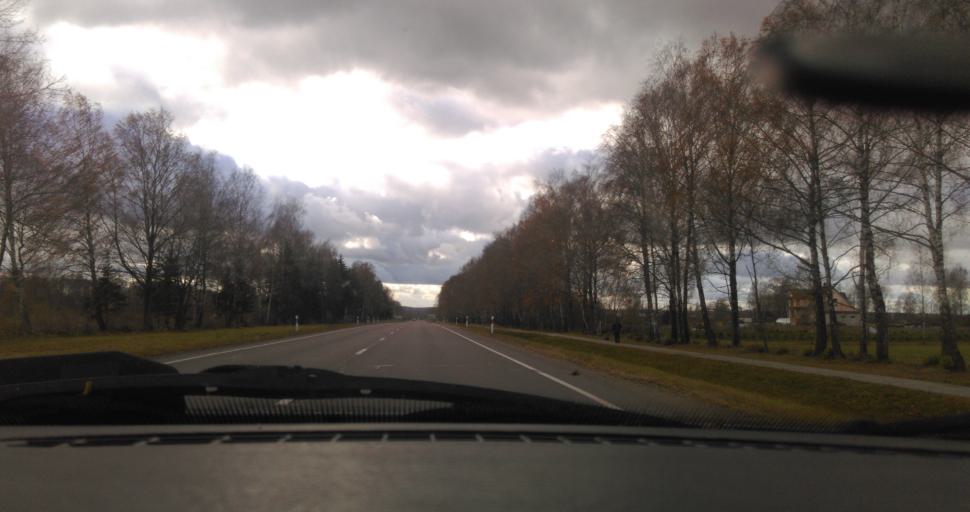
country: LT
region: Utenos apskritis
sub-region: Utena
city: Utena
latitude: 55.5111
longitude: 25.6392
